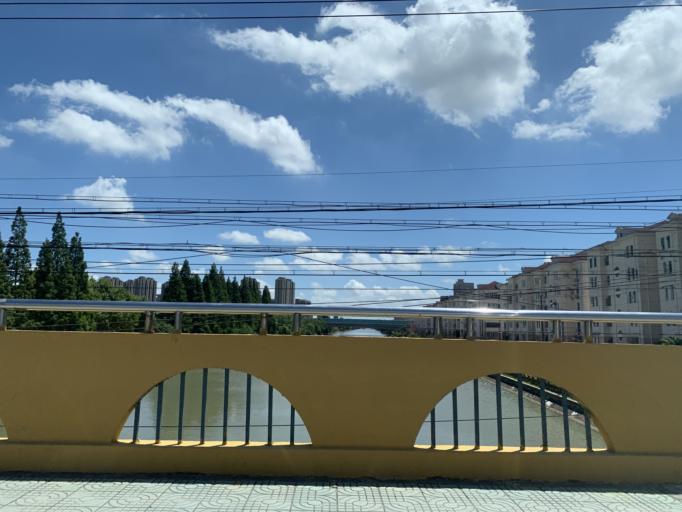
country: CN
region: Shanghai Shi
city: Huamu
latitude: 31.1759
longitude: 121.5350
